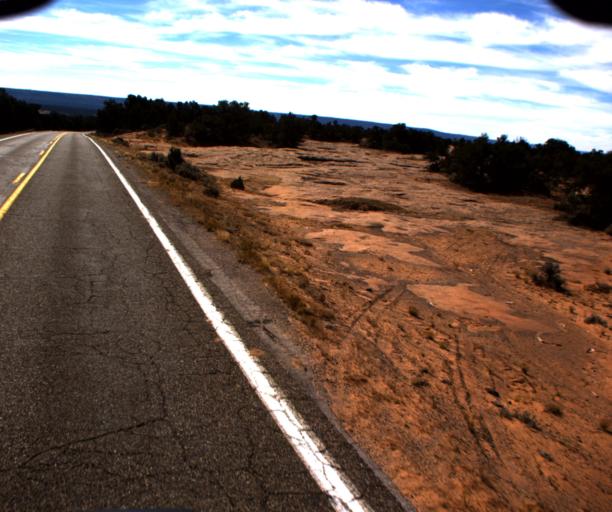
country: US
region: Arizona
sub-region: Navajo County
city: Kayenta
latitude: 36.6330
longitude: -110.5095
